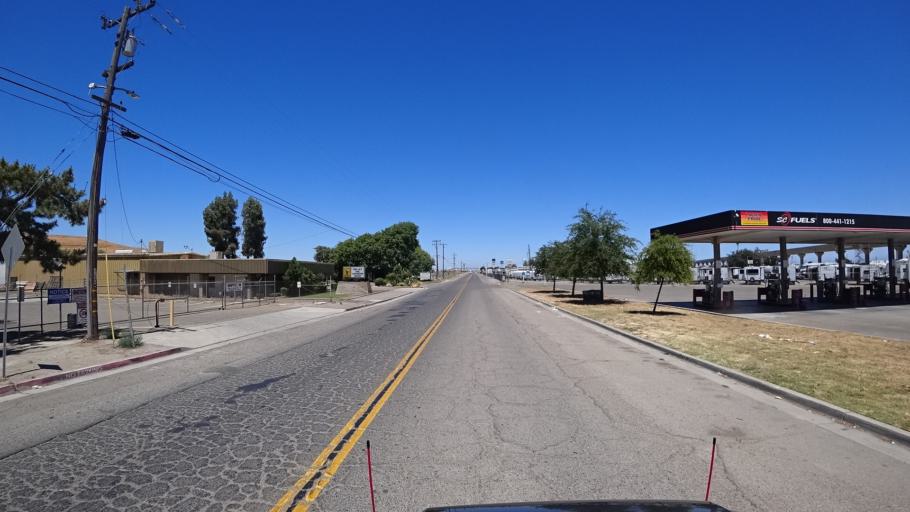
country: US
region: California
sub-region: Fresno County
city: Easton
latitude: 36.6882
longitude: -119.7557
